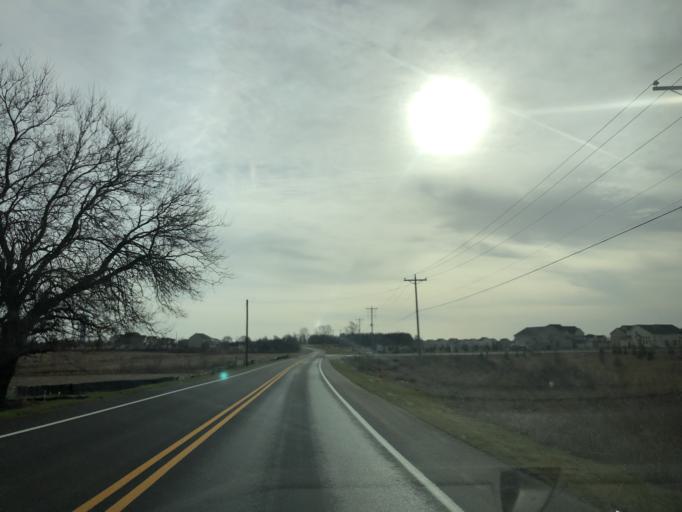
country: US
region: Delaware
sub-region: New Castle County
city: Delaware City
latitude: 39.5226
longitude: -75.6606
